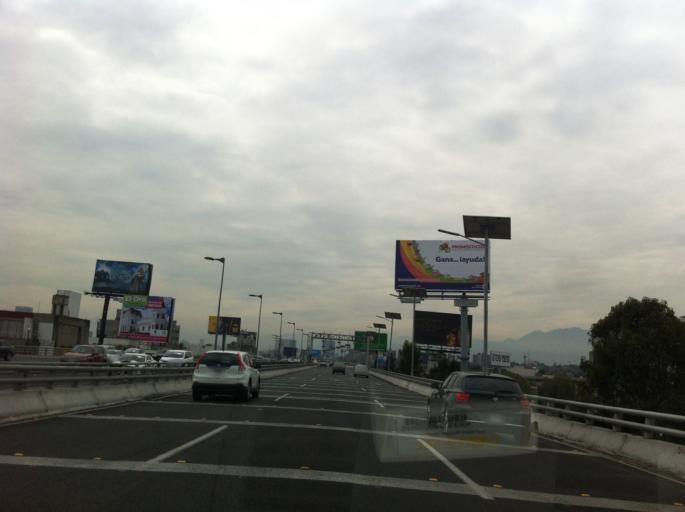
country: MX
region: Mexico City
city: Alvaro Obregon
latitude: 19.3819
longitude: -99.1910
